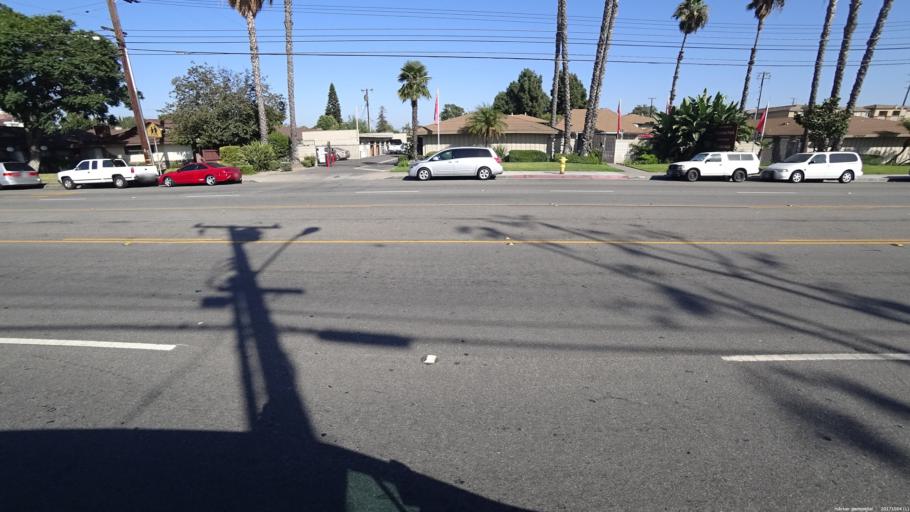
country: US
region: California
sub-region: Orange County
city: Stanton
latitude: 33.8044
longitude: -117.9758
